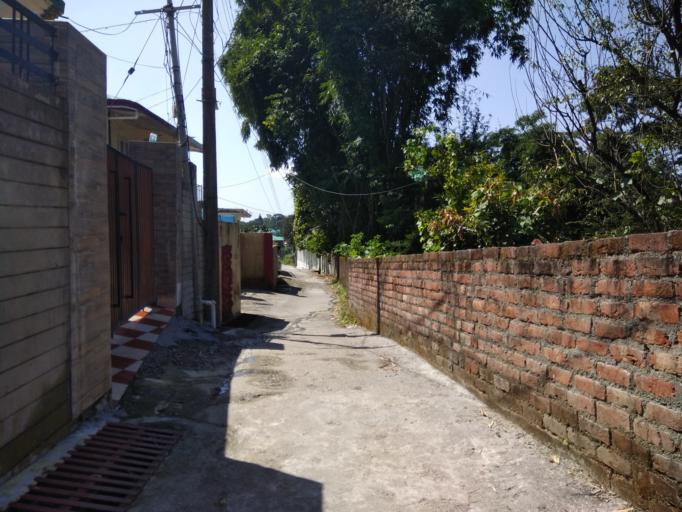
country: IN
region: Himachal Pradesh
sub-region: Kangra
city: Palampur
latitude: 32.1233
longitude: 76.5400
